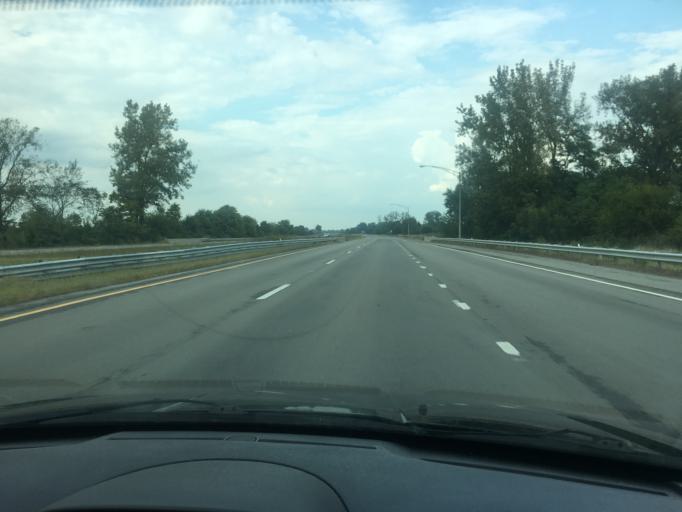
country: US
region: Ohio
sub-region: Clark County
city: Northridge
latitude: 39.9919
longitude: -83.8117
